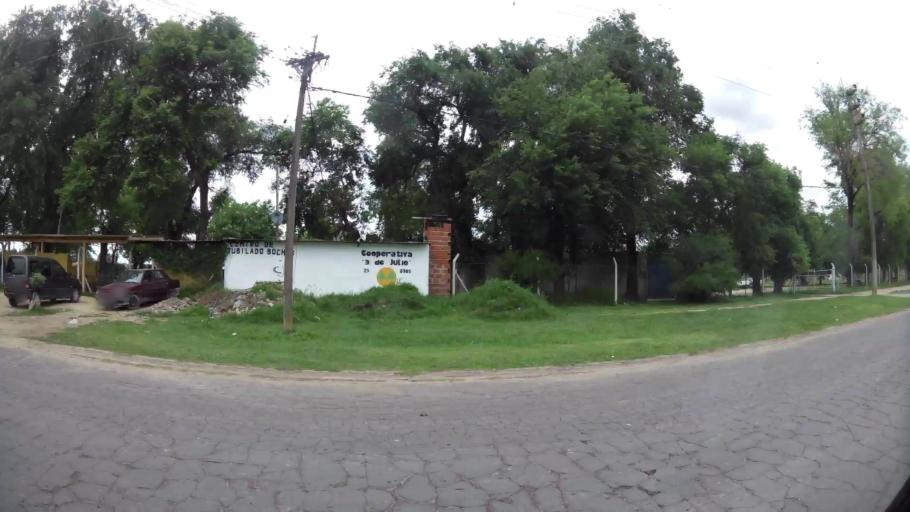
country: AR
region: Buenos Aires
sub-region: Partido de Zarate
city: Zarate
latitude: -34.1174
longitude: -59.0162
